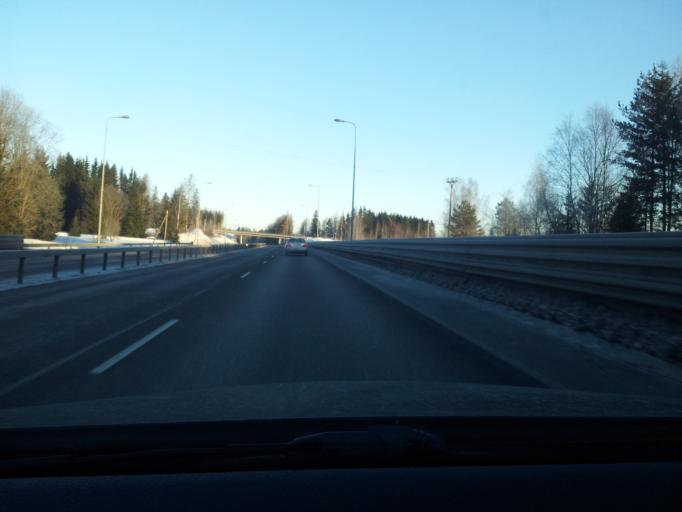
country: FI
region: Uusimaa
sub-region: Helsinki
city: Vihti
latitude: 60.3126
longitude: 24.3486
